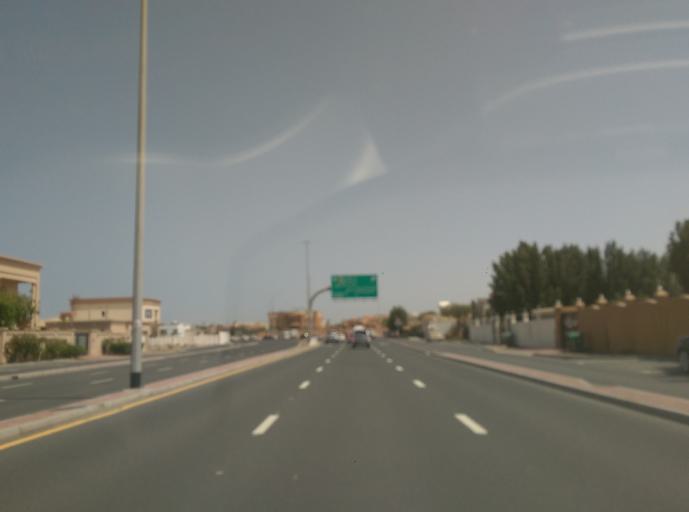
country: AE
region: Dubai
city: Dubai
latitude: 25.0922
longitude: 55.2029
